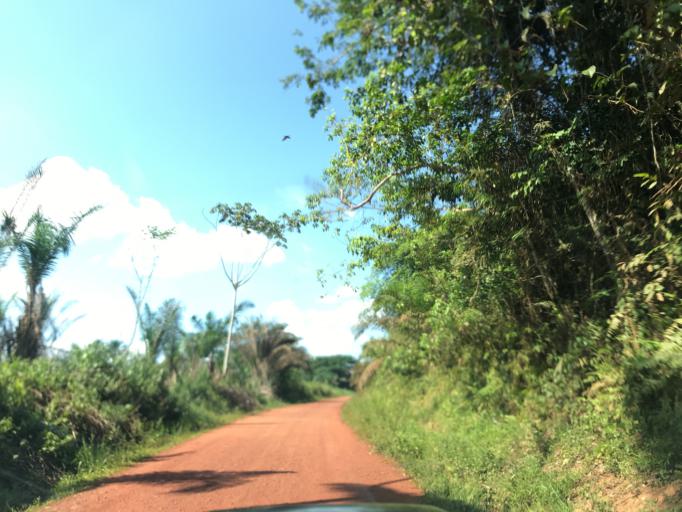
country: CD
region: Eastern Province
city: Kisangani
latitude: 1.2067
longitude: 25.2612
